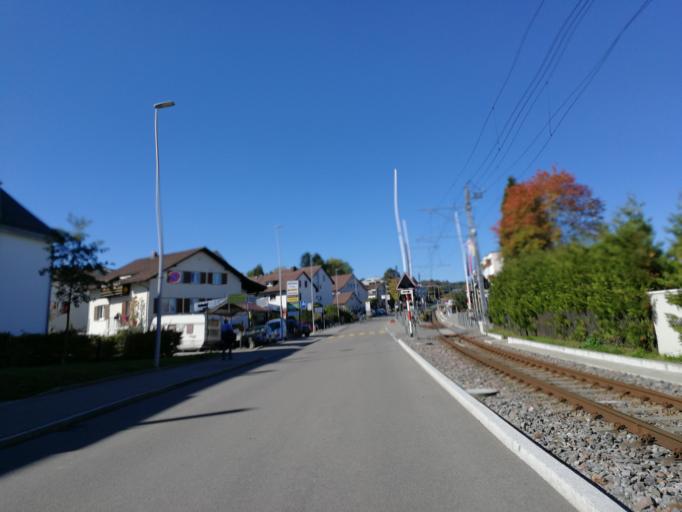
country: CH
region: Zurich
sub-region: Bezirk Uster
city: Aesch
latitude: 47.3219
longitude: 8.6610
